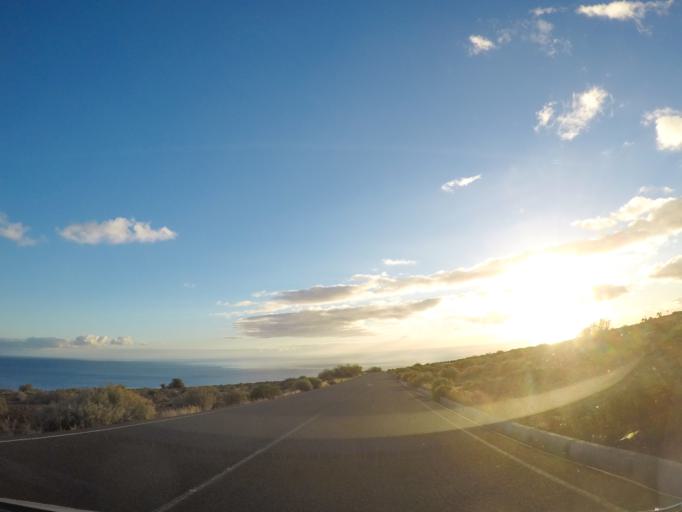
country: ES
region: Canary Islands
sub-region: Provincia de Santa Cruz de Tenerife
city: Alajero
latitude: 28.0363
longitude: -17.2196
